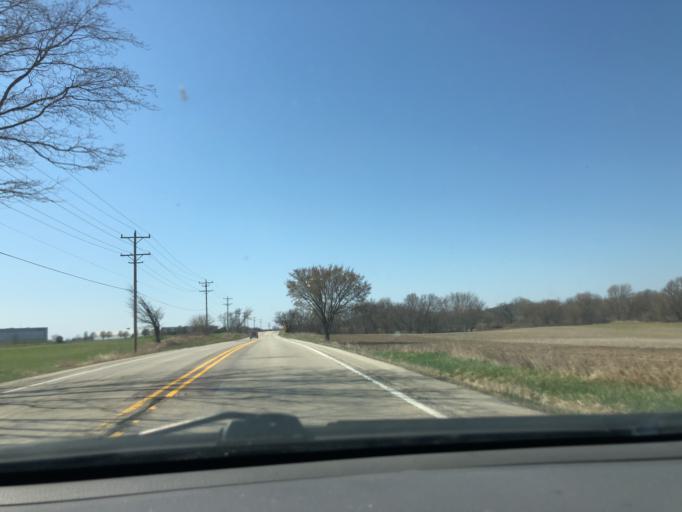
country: US
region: Illinois
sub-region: Kane County
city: Hampshire
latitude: 42.1331
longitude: -88.4960
